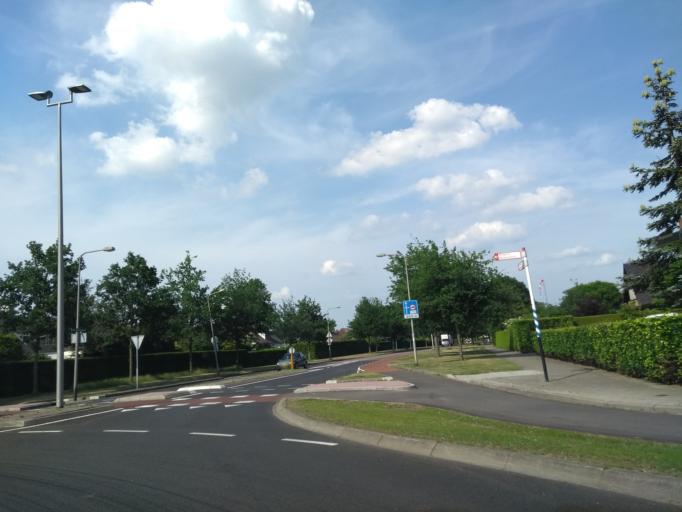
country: DE
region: Lower Saxony
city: Nordhorn
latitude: 52.3781
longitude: 6.9963
